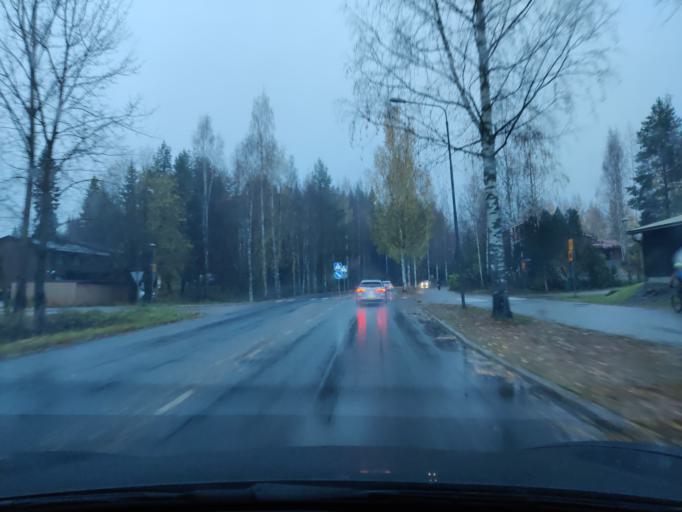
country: FI
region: Northern Savo
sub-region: Kuopio
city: Kuopio
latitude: 62.8524
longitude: 27.6403
